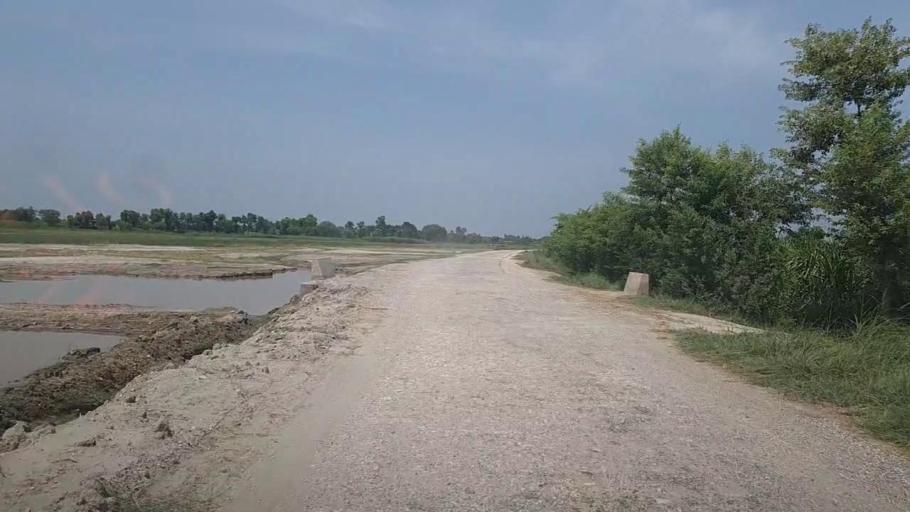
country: PK
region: Sindh
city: Ubauro
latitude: 28.1861
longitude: 69.7694
